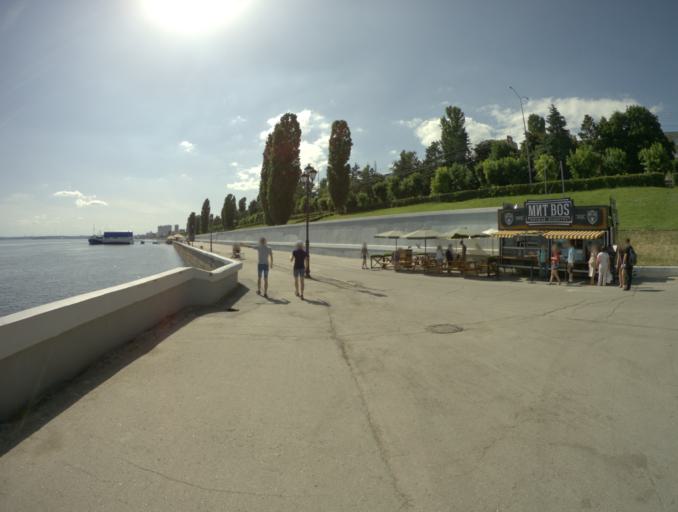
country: RU
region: Saratov
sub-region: Saratovskiy Rayon
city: Saratov
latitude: 51.5251
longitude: 46.0506
